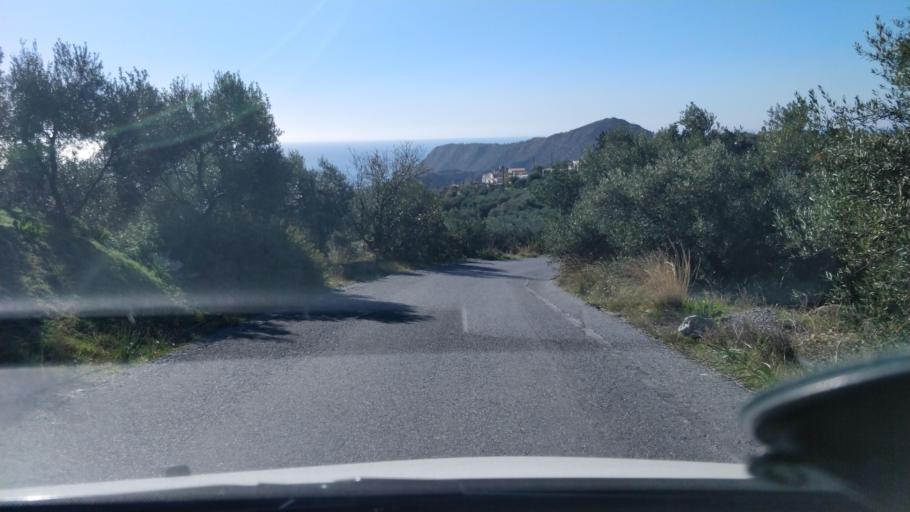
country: GR
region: Crete
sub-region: Nomos Lasithiou
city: Gra Liyia
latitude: 35.0208
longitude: 25.5569
